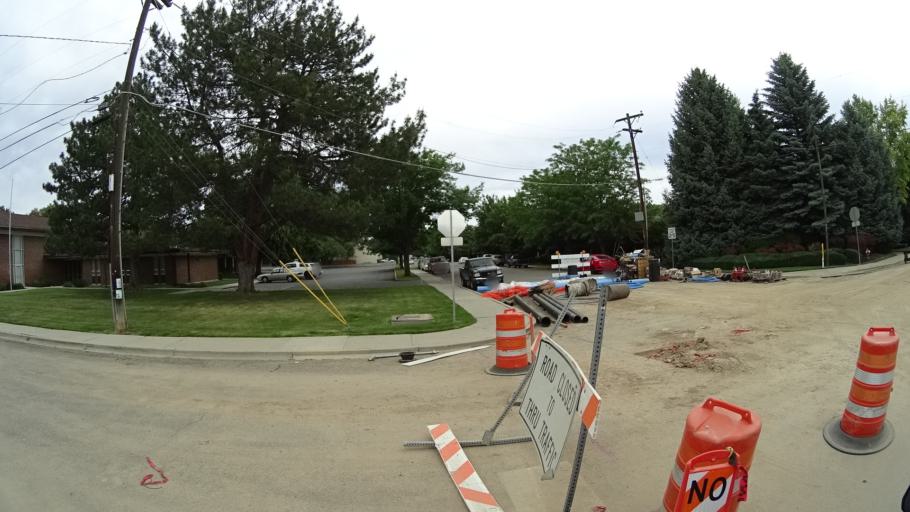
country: US
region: Idaho
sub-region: Ada County
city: Boise
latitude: 43.5807
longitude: -116.2188
